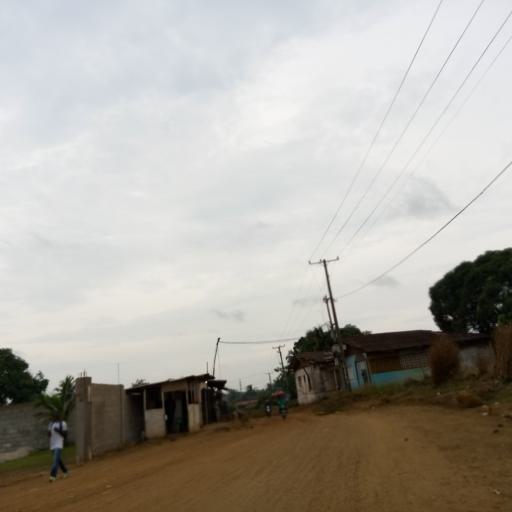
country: LR
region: Montserrado
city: Monrovia
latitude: 6.2944
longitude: -10.6787
